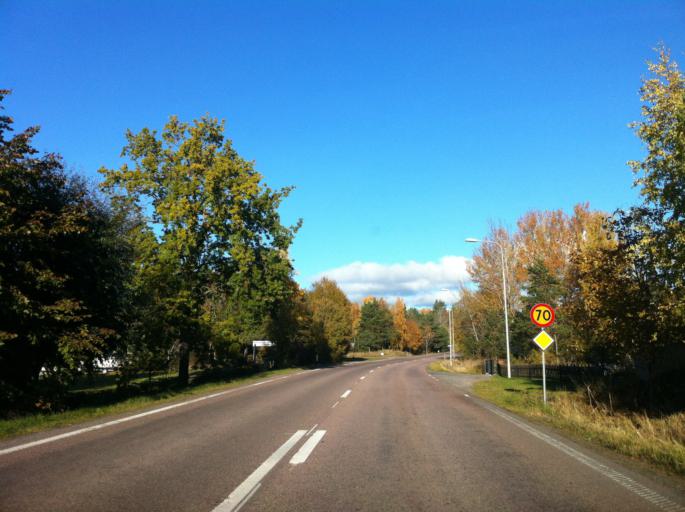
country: SE
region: Uppsala
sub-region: Osthammars Kommun
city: Oregrund
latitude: 60.3294
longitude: 18.4271
